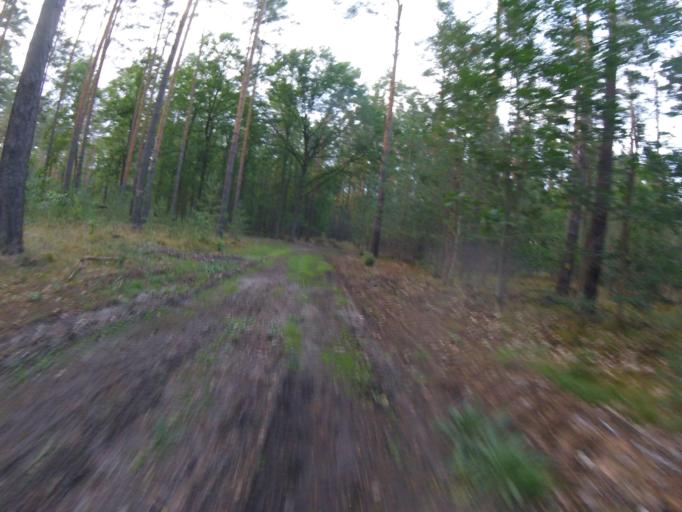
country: DE
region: Brandenburg
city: Gross Koris
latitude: 52.2026
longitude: 13.6860
